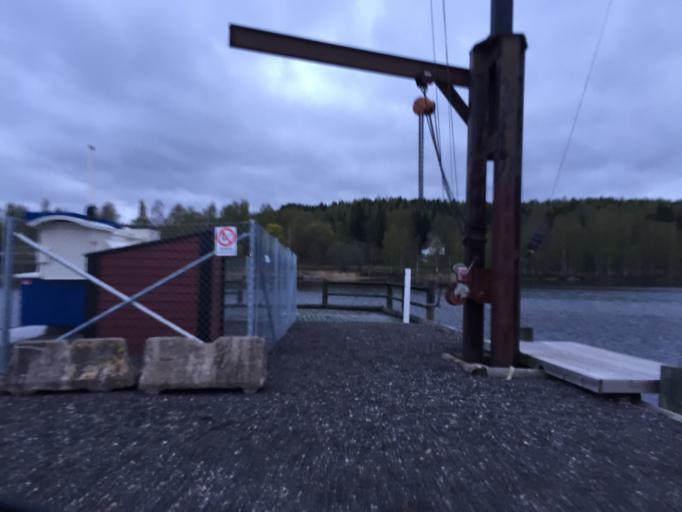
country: SE
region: Dalarna
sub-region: Ludvika Kommun
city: Ludvika
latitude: 60.1394
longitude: 15.1693
